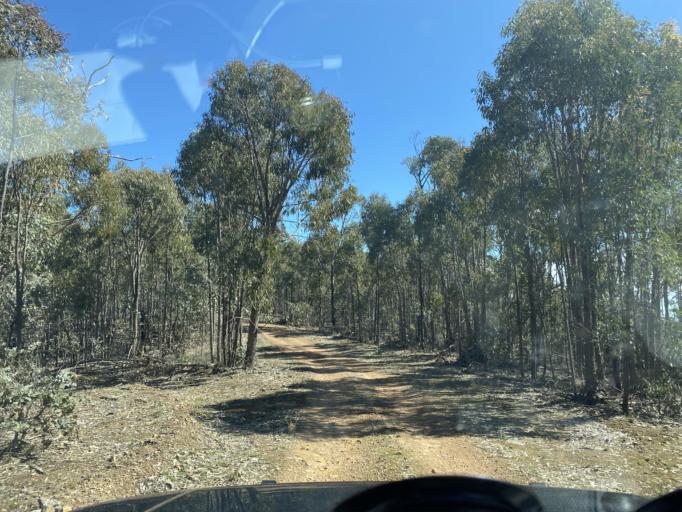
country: AU
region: Victoria
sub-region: Benalla
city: Benalla
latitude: -36.7260
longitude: 146.1819
